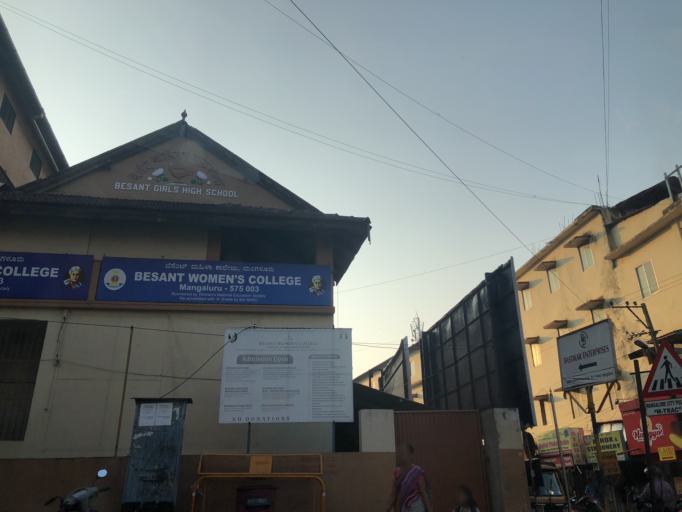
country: IN
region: Karnataka
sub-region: Dakshina Kannada
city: Mangalore
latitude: 12.8776
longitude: 74.8413
